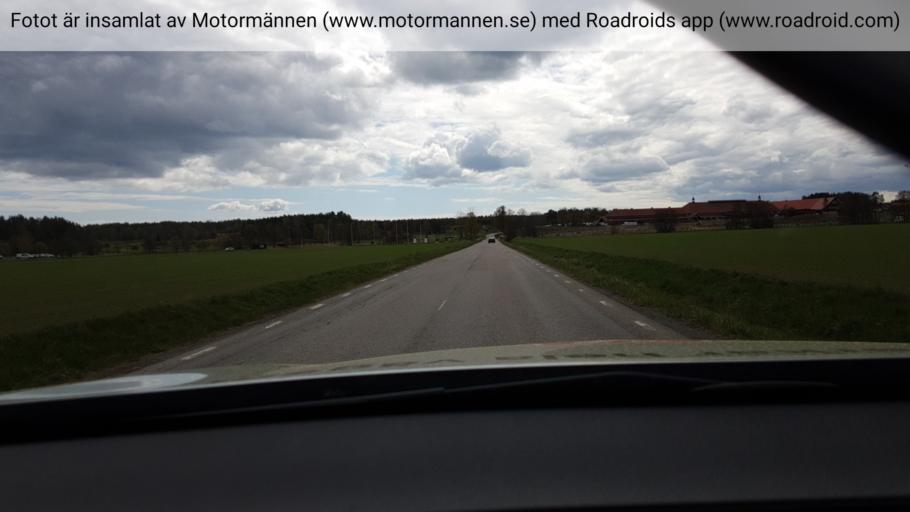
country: SE
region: Stockholm
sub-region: Haninge Kommun
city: Haninge
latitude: 59.1083
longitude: 18.1879
